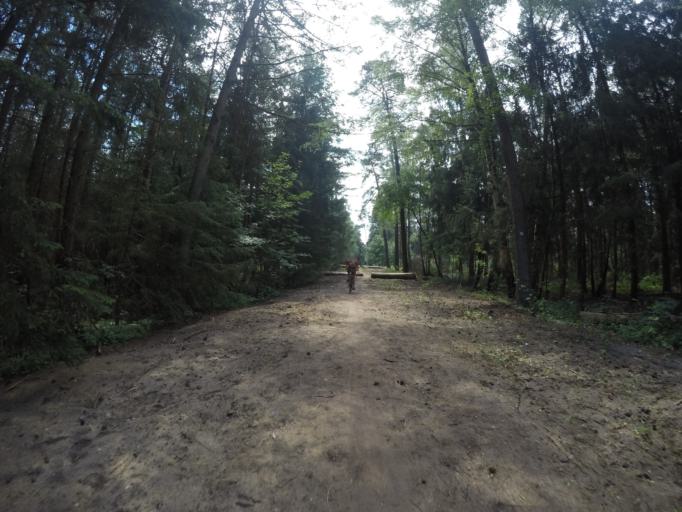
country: DE
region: Lower Saxony
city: Handeloh
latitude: 53.2878
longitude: 9.8451
